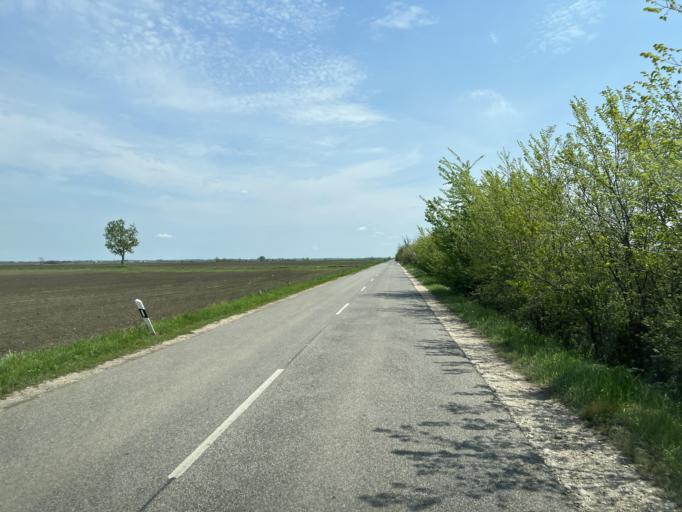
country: HU
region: Pest
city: Tapioszentmarton
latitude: 47.2926
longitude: 19.7538
